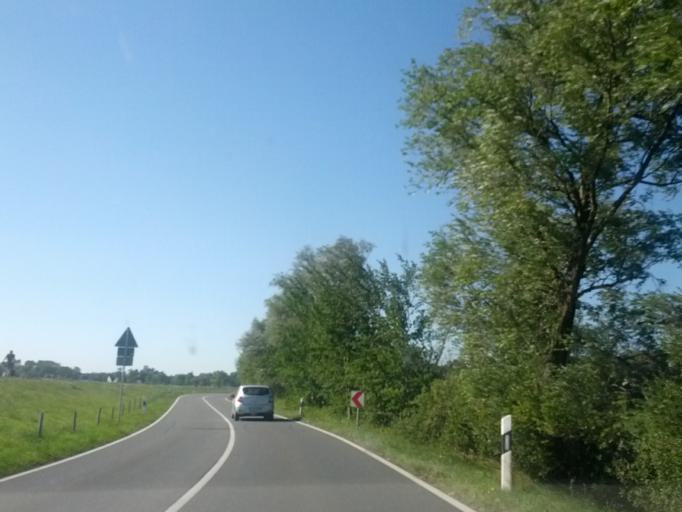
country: DE
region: Mecklenburg-Vorpommern
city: Ostseebad Gohren
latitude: 54.3267
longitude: 13.7079
